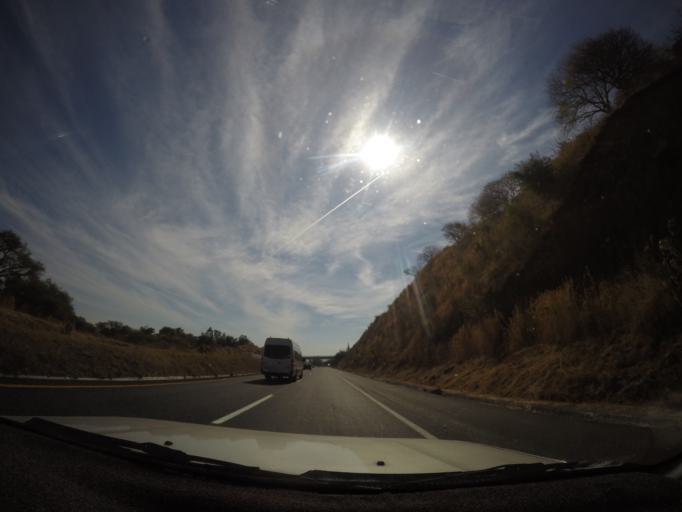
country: MX
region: Jalisco
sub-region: Ocotlan
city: Joconoxtle (La Tuna)
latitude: 20.3796
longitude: -102.6912
